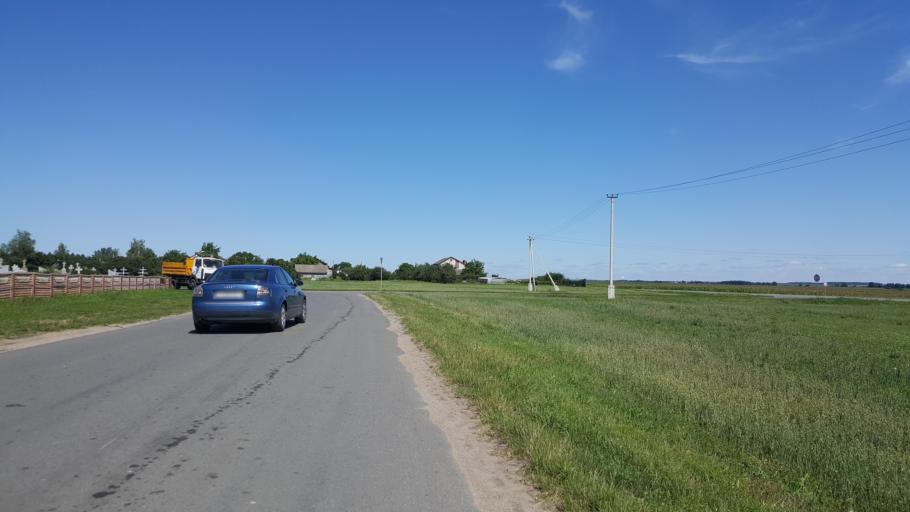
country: BY
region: Brest
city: Charnawchytsy
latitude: 52.2197
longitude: 23.7485
